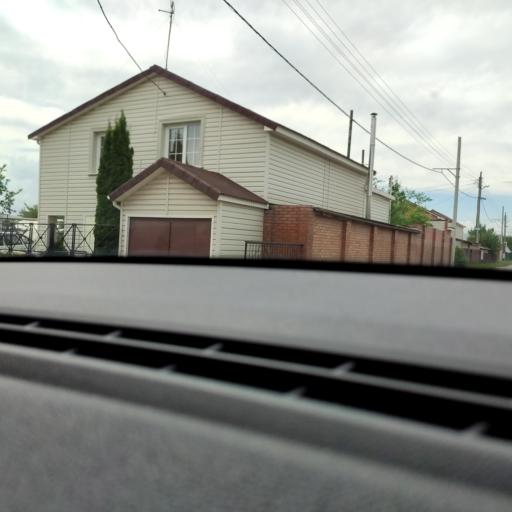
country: RU
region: Samara
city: Podstepki
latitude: 53.5087
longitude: 49.1760
